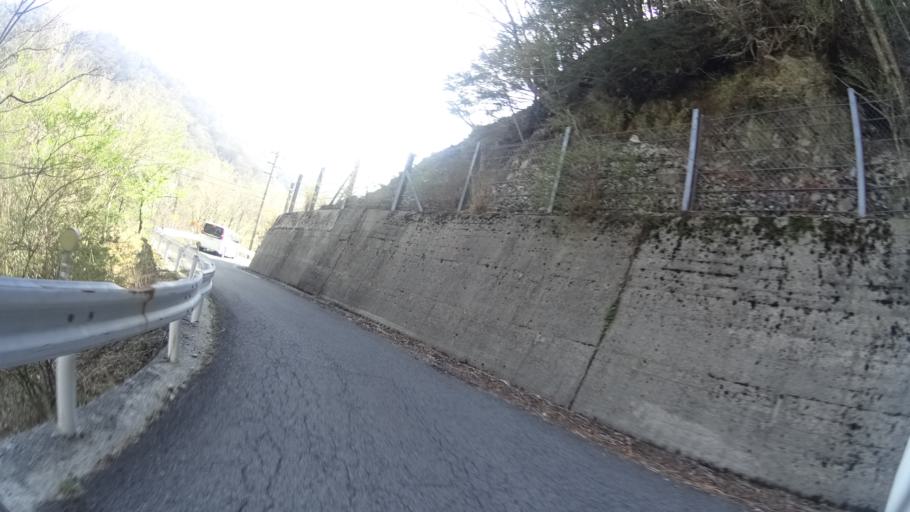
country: JP
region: Tokushima
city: Wakimachi
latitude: 33.8671
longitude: 134.0793
